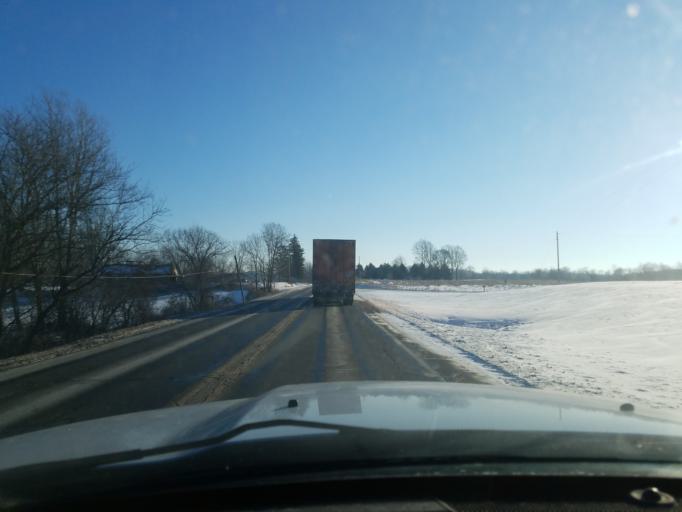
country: US
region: Indiana
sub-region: Noble County
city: Rome City
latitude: 41.4528
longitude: -85.3670
